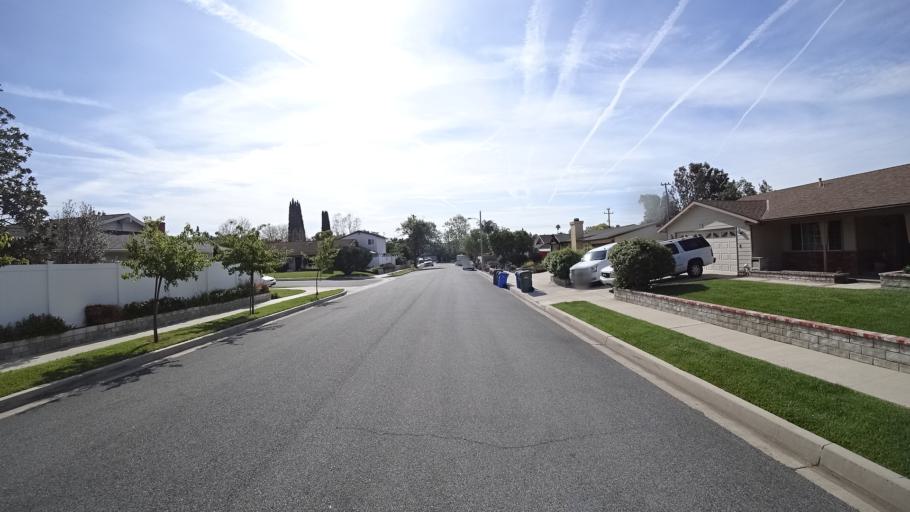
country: US
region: California
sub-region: Ventura County
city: Thousand Oaks
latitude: 34.1988
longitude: -118.8755
